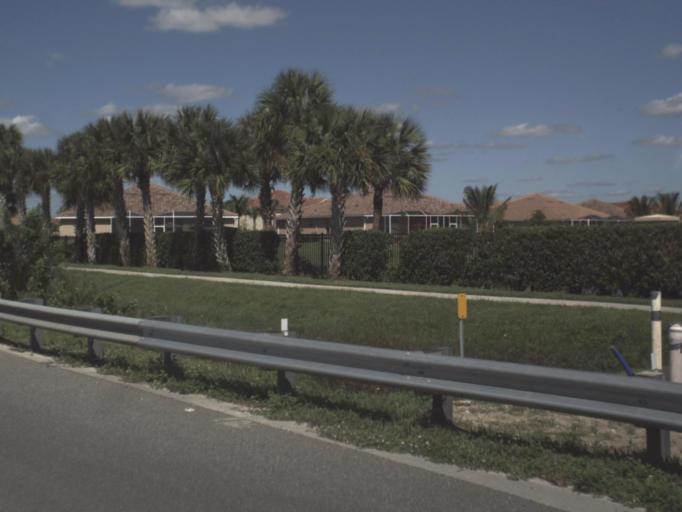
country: US
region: Florida
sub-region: Collier County
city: Lely Resort
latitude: 26.0413
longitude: -81.6646
